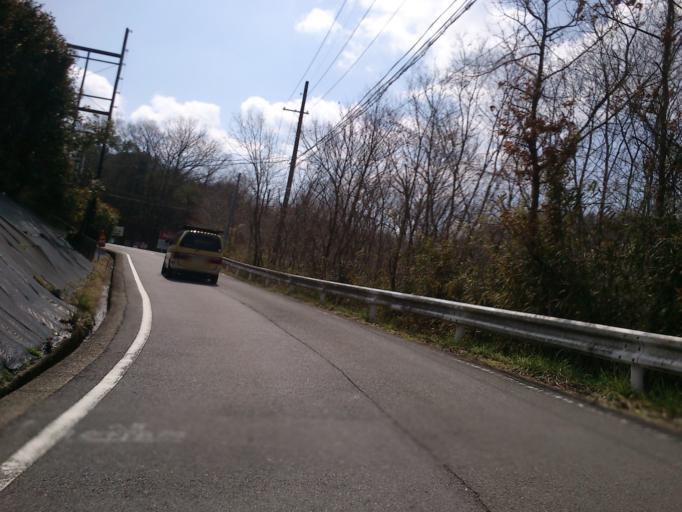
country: JP
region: Mie
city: Ueno-ebisumachi
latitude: 34.7489
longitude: 136.0220
